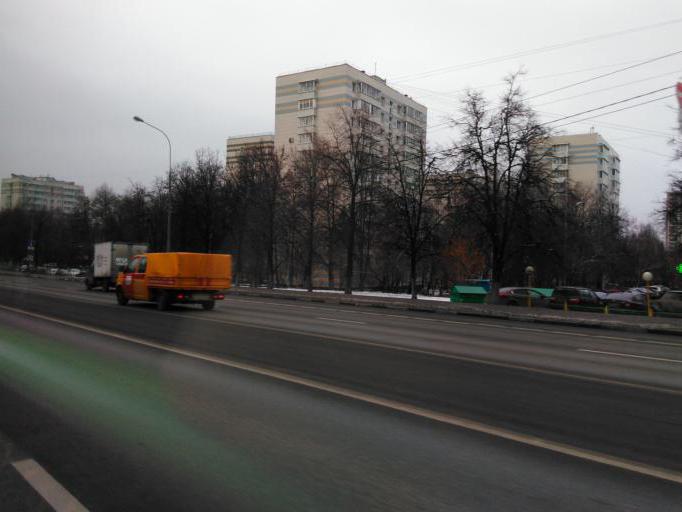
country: RU
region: Moscow
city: Zyuzino
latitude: 55.6500
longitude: 37.5599
